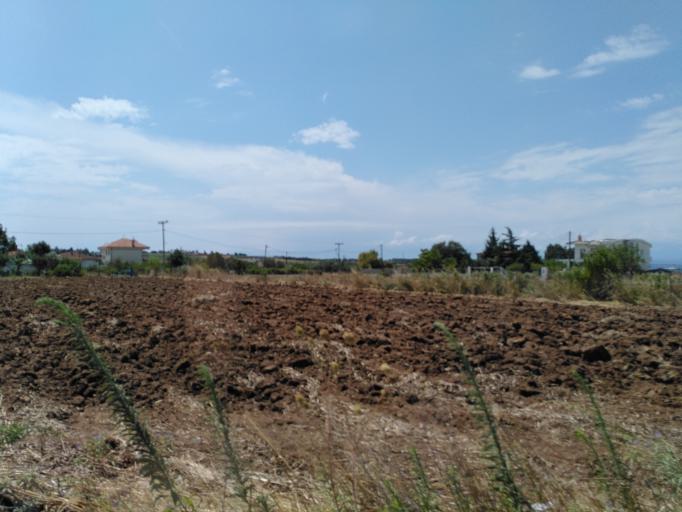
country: GR
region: Central Macedonia
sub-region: Nomos Thessalonikis
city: Agia Triada
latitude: 40.4931
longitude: 22.8557
